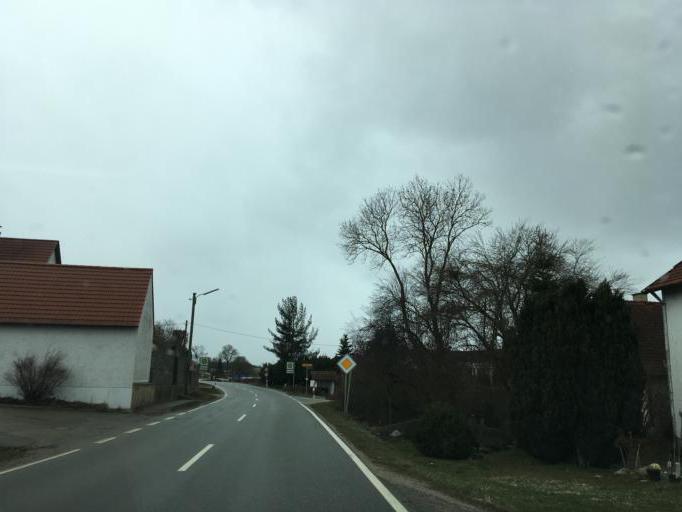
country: DE
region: Bavaria
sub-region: Upper Bavaria
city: Rudelzhausen
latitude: 48.5841
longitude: 11.7597
